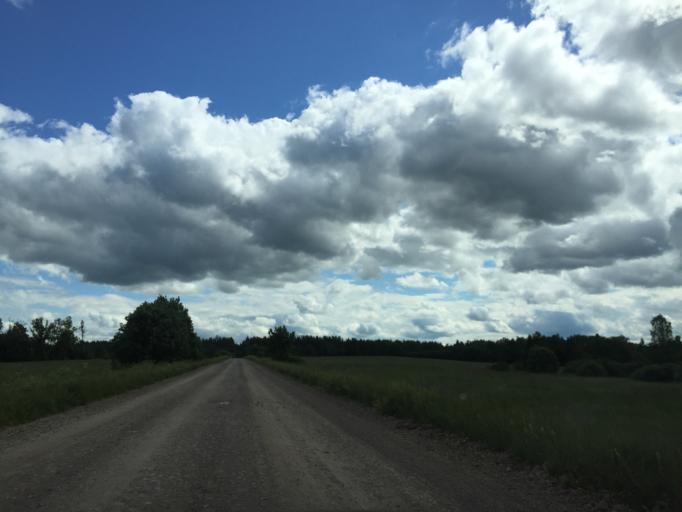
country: LV
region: Vecumnieki
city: Vecumnieki
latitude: 56.5013
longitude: 24.4065
